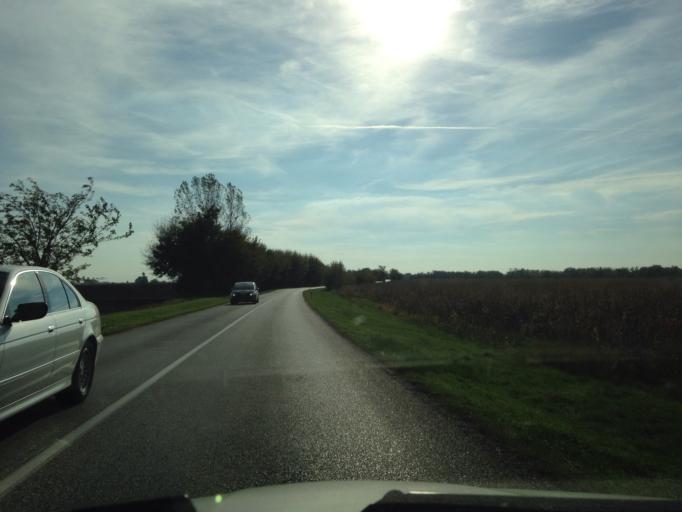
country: SK
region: Nitriansky
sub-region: Okres Komarno
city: Hurbanovo
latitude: 47.8249
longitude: 18.2335
